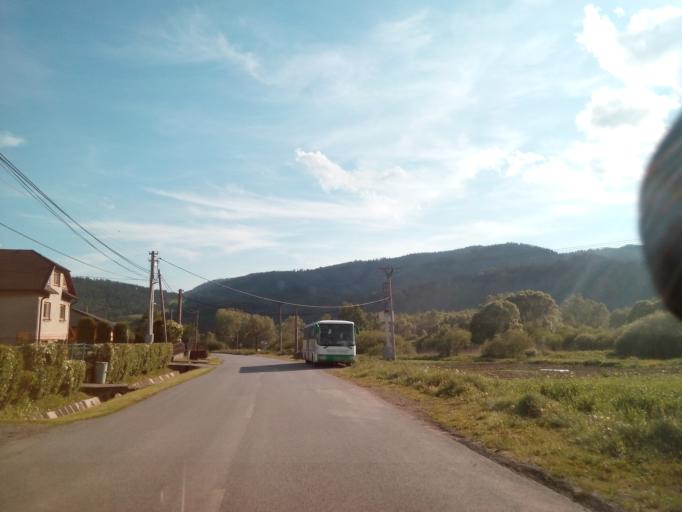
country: SK
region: Presovsky
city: Lipany
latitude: 49.0512
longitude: 20.9491
